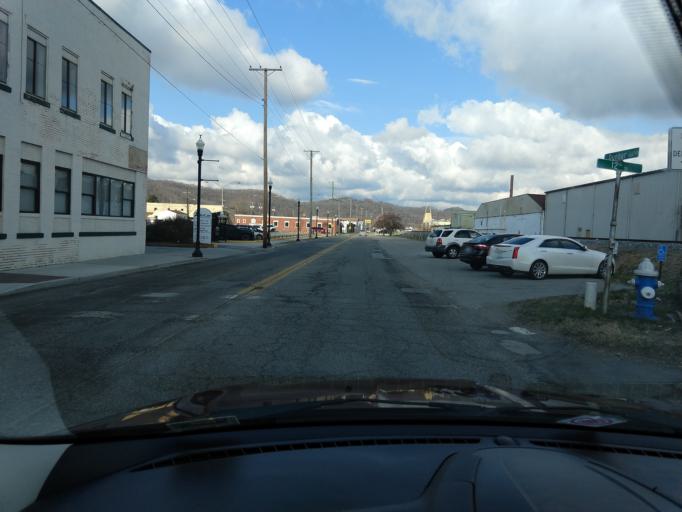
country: US
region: West Virginia
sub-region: Kanawha County
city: Dunbar
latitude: 38.3605
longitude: -81.7402
